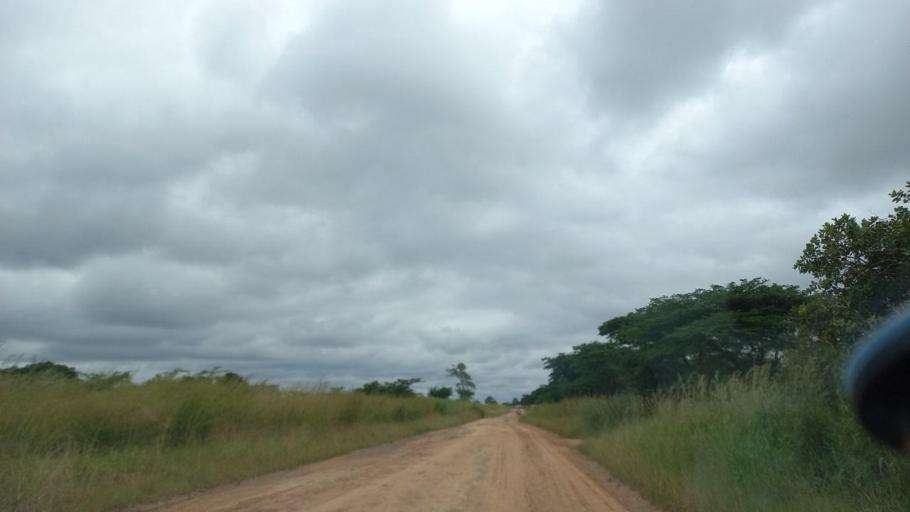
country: ZM
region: Lusaka
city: Lusaka
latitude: -15.2256
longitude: 28.3363
